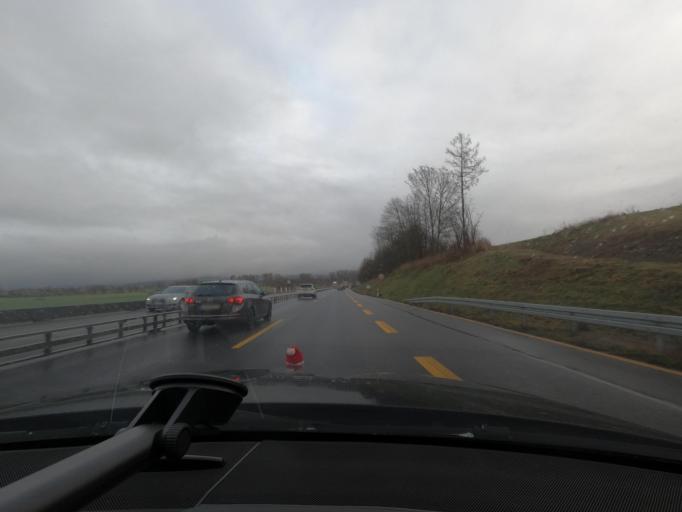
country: DE
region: Lower Saxony
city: Hillerse
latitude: 51.7195
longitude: 9.9449
